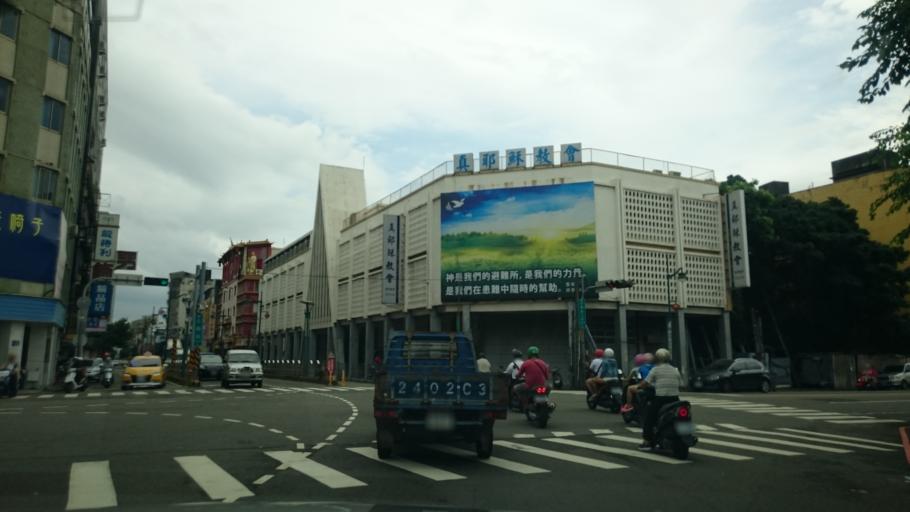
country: TW
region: Taiwan
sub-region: Taichung City
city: Taichung
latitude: 24.1473
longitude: 120.6787
